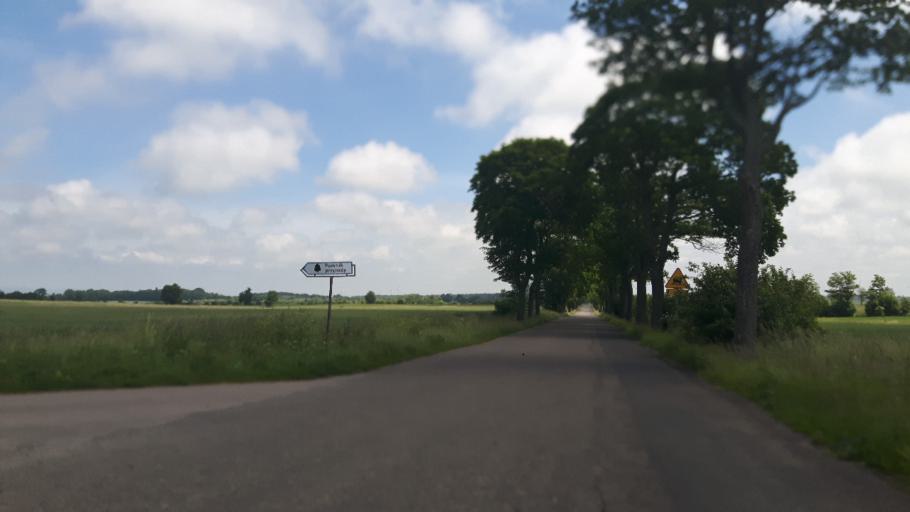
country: PL
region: West Pomeranian Voivodeship
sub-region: Powiat slawienski
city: Slawno
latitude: 54.5086
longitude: 16.5981
